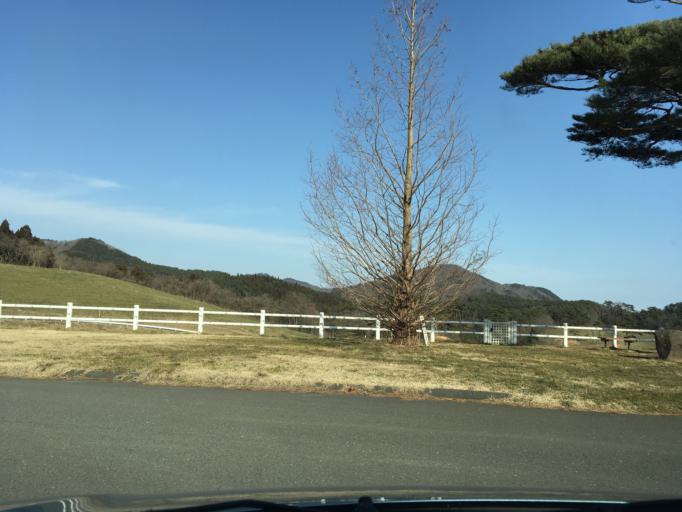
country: JP
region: Iwate
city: Ichinoseki
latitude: 38.7988
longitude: 141.4439
